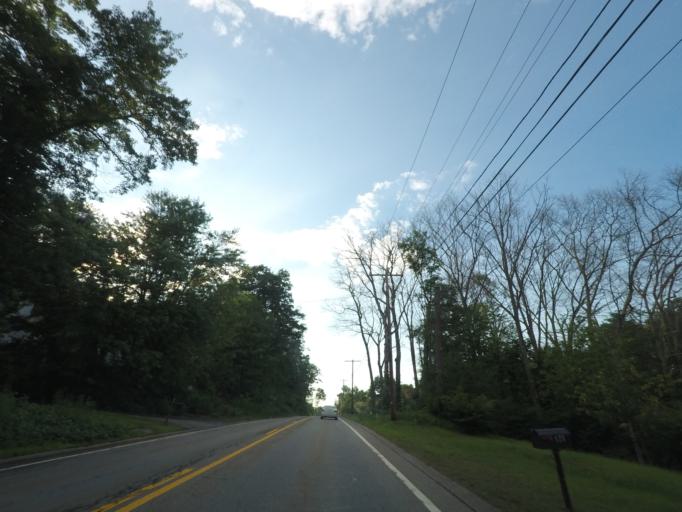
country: US
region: Connecticut
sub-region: Windham County
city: Quinebaug
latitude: 42.0409
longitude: -71.9742
